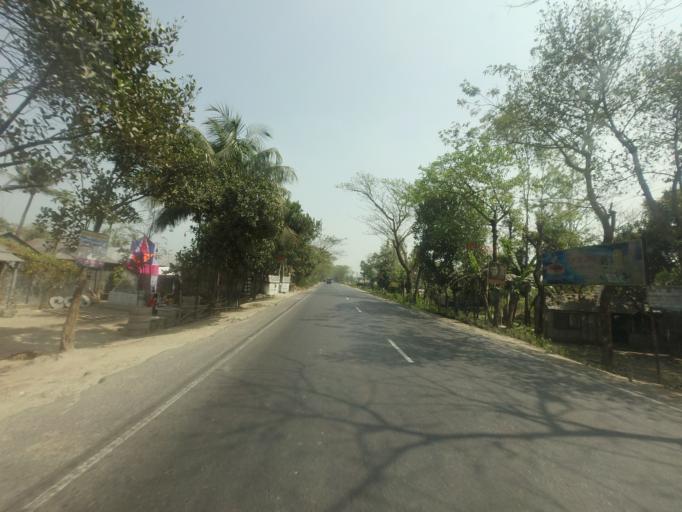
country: BD
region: Dhaka
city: Bhairab Bazar
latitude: 24.0469
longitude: 91.0852
